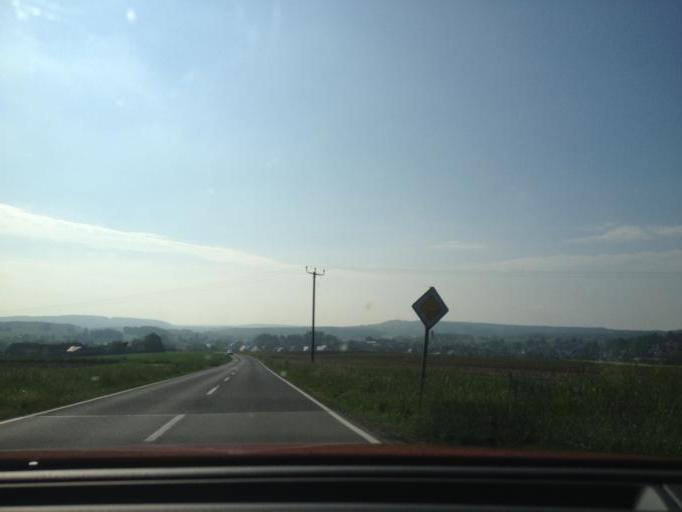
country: DE
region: Bavaria
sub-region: Upper Palatinate
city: Kirchenthumbach
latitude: 49.7566
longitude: 11.7111
